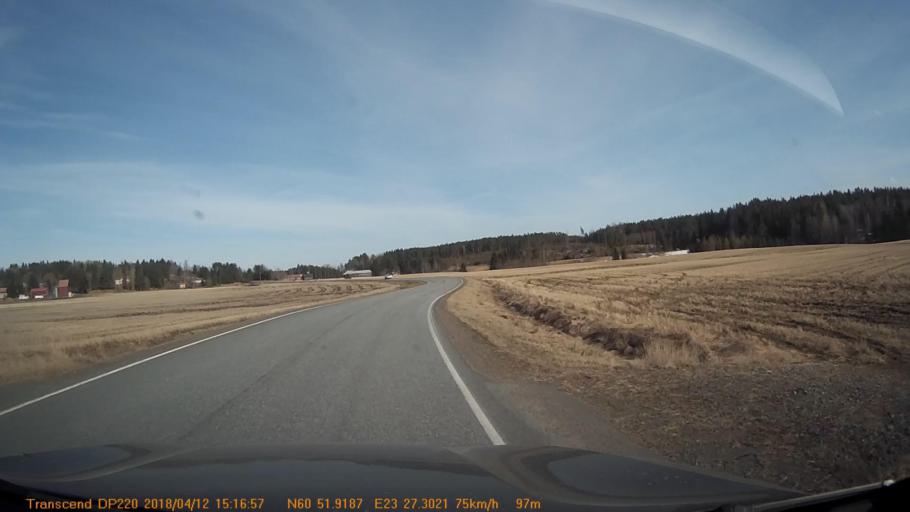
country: FI
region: Haeme
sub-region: Forssa
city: Jokioinen
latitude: 60.8653
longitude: 23.4558
